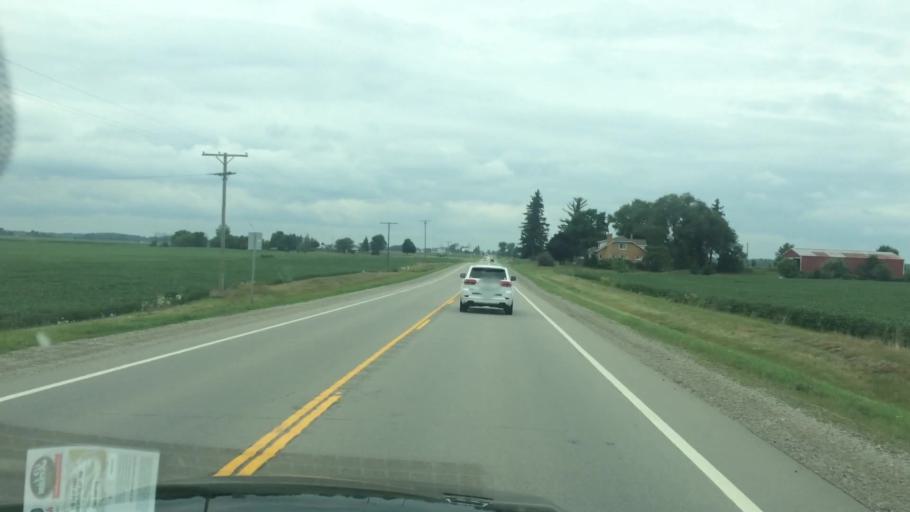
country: US
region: Michigan
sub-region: Sanilac County
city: Marlette
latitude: 43.3942
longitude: -83.0864
